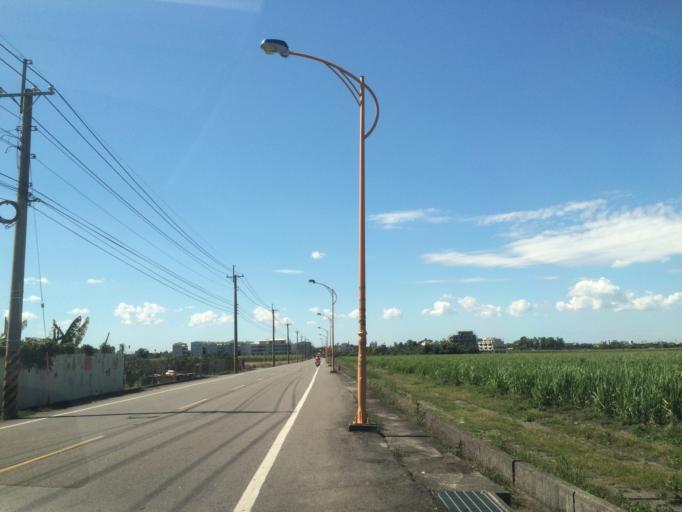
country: TW
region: Taiwan
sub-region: Yunlin
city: Douliu
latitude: 23.7031
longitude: 120.5849
